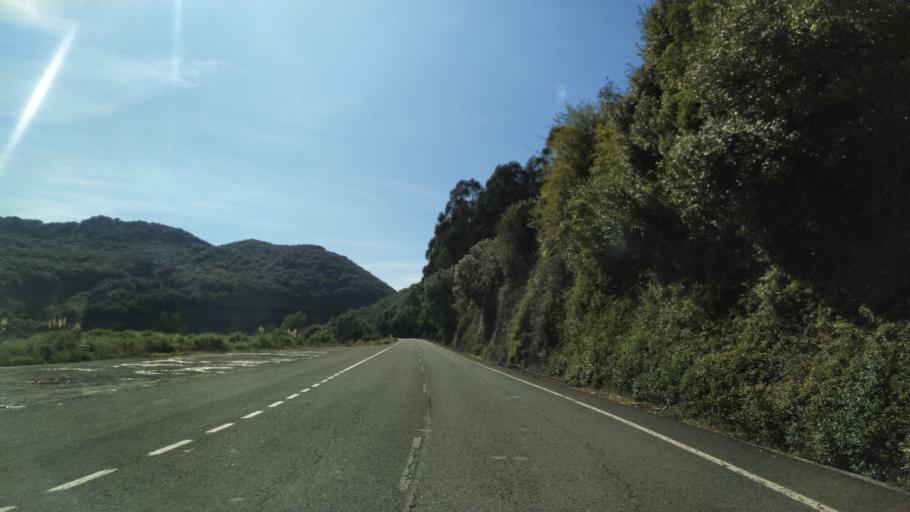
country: ES
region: Cantabria
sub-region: Provincia de Cantabria
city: Liendo
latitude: 43.3937
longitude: -3.3455
